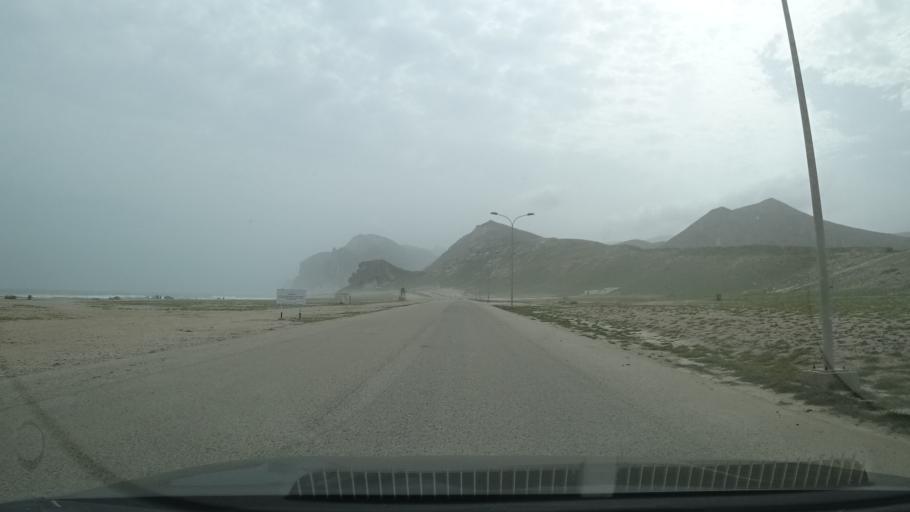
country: OM
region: Zufar
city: Salalah
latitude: 16.8803
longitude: 53.7739
